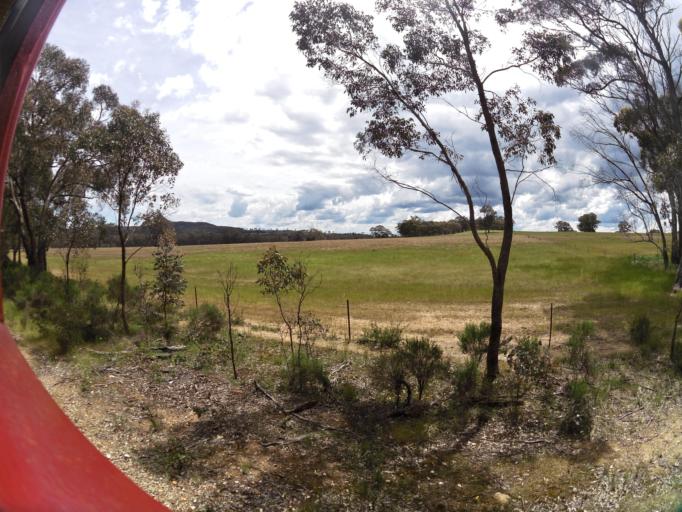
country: AU
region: Victoria
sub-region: Mount Alexander
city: Castlemaine
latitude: -36.9942
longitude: 144.0986
